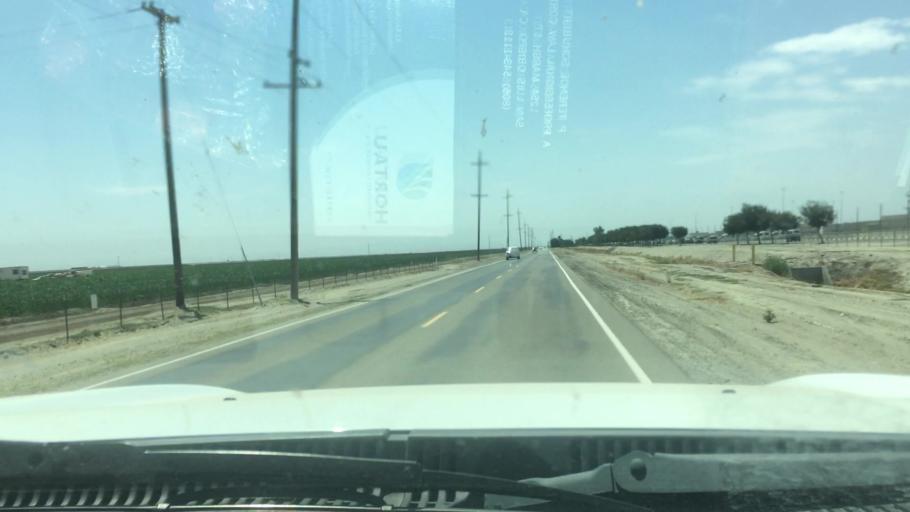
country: US
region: California
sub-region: Kings County
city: Corcoran
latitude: 36.0508
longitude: -119.5456
